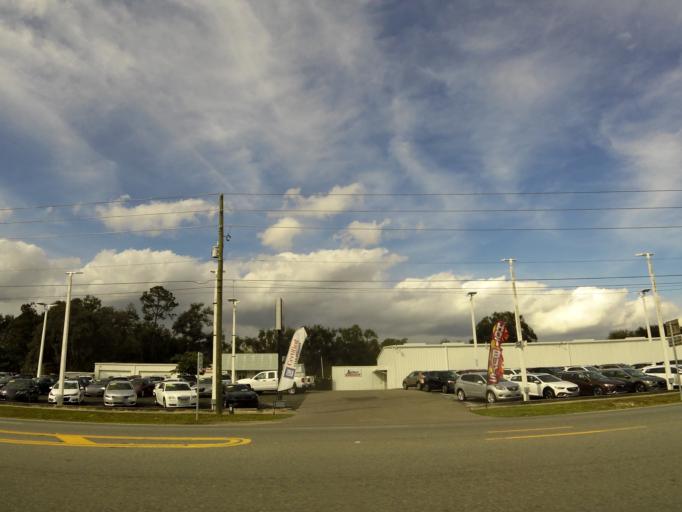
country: US
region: Florida
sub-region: Volusia County
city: De Land Southwest
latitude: 28.9989
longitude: -81.3040
